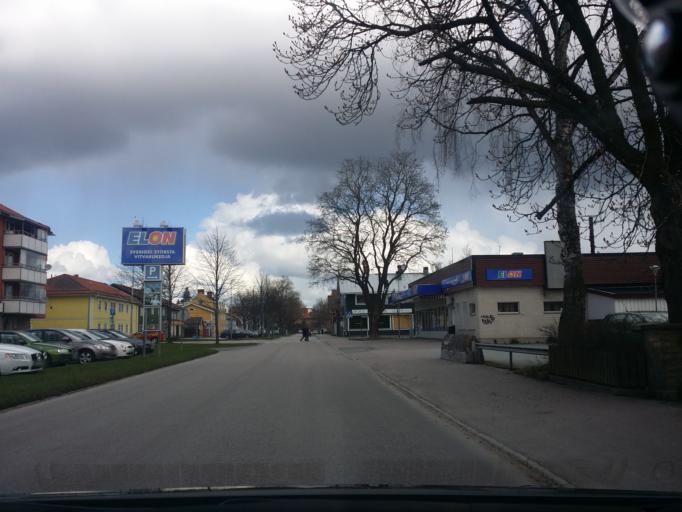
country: SE
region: Vaestmanland
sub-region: Sala Kommun
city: Sala
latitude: 59.9179
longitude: 16.6110
